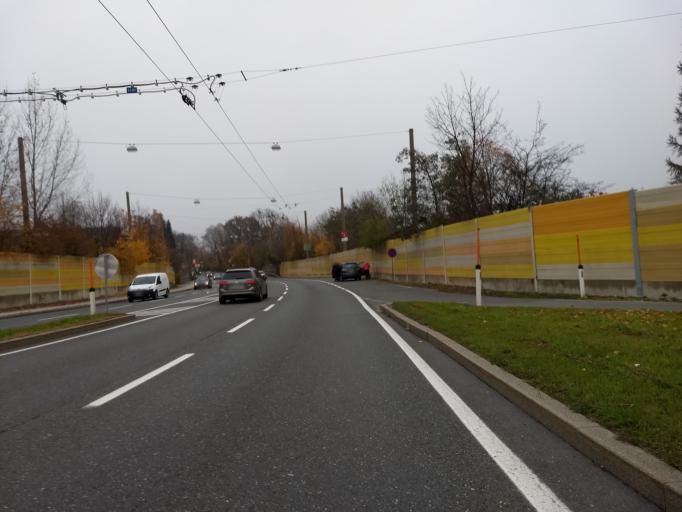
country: AT
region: Salzburg
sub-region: Politischer Bezirk Salzburg-Umgebung
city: Bergheim
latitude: 47.8260
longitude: 13.0120
